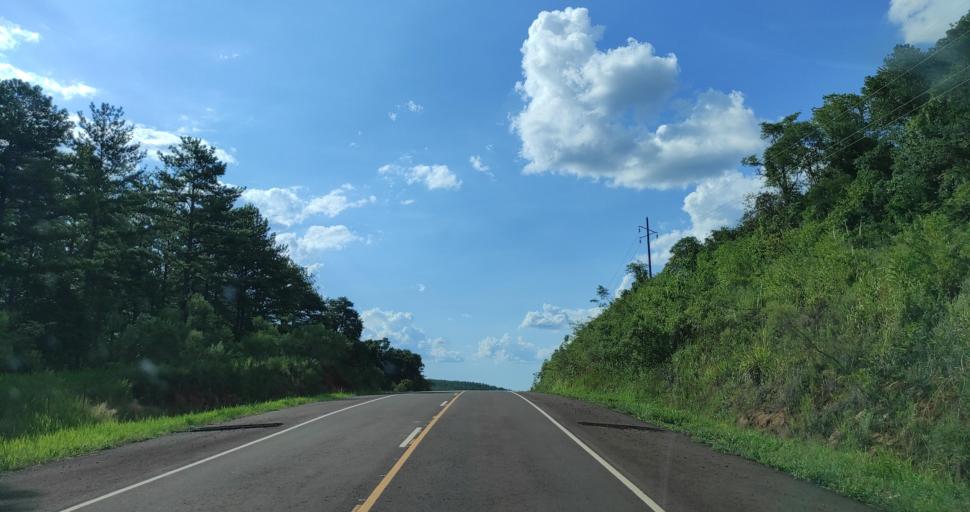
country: AR
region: Misiones
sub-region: Departamento de San Pedro
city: San Pedro
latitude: -26.3578
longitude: -53.9554
